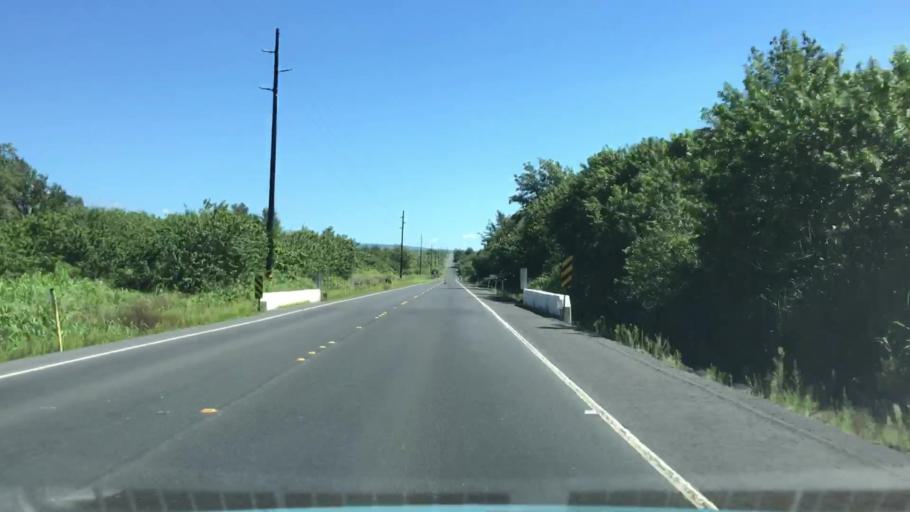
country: US
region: Hawaii
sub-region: Hawaii County
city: Pahala
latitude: 19.2482
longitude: -155.4442
